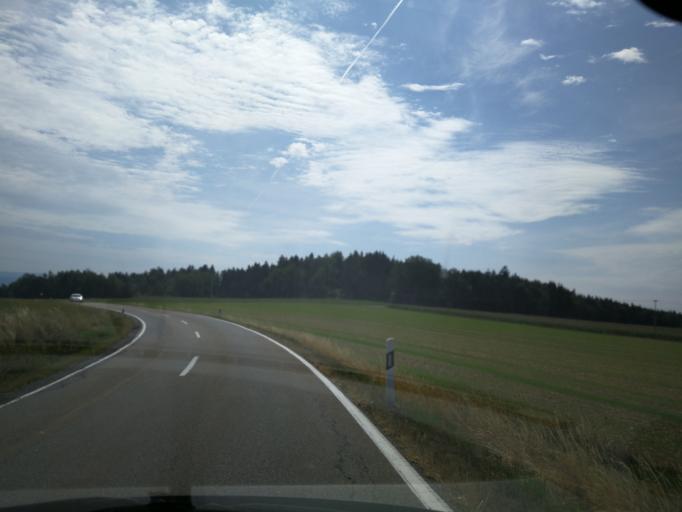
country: DE
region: Bavaria
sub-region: Lower Bavaria
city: Falkenfels
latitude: 49.0515
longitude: 12.5865
